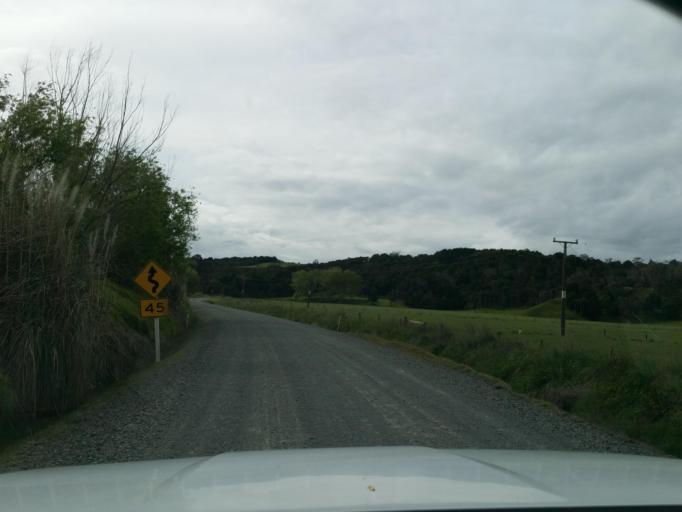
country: NZ
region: Northland
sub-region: Kaipara District
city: Dargaville
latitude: -35.9020
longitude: 173.9211
